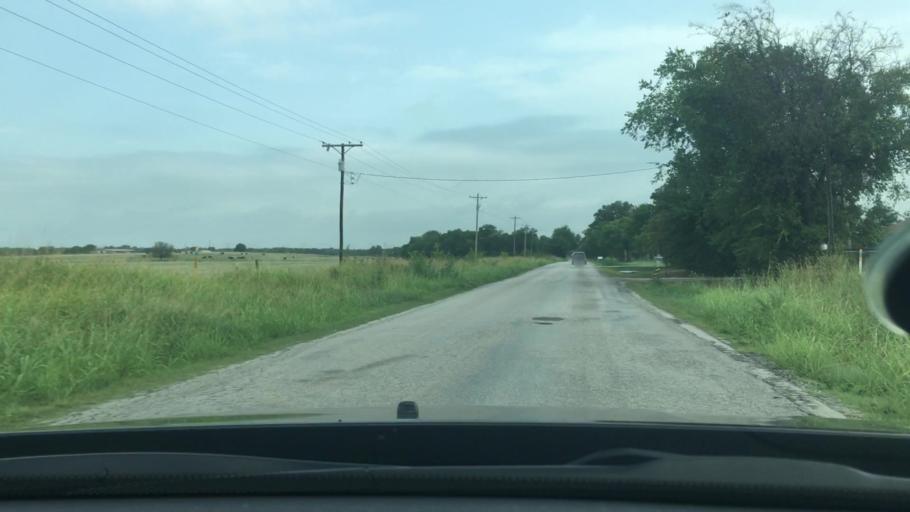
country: US
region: Oklahoma
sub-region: Carter County
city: Lone Grove
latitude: 34.2088
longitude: -97.2650
